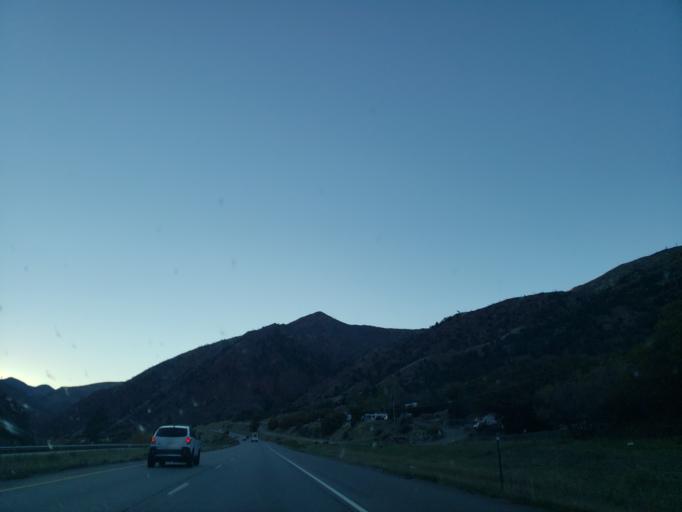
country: US
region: Colorado
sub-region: Garfield County
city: Glenwood Springs
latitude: 39.5608
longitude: -107.3774
